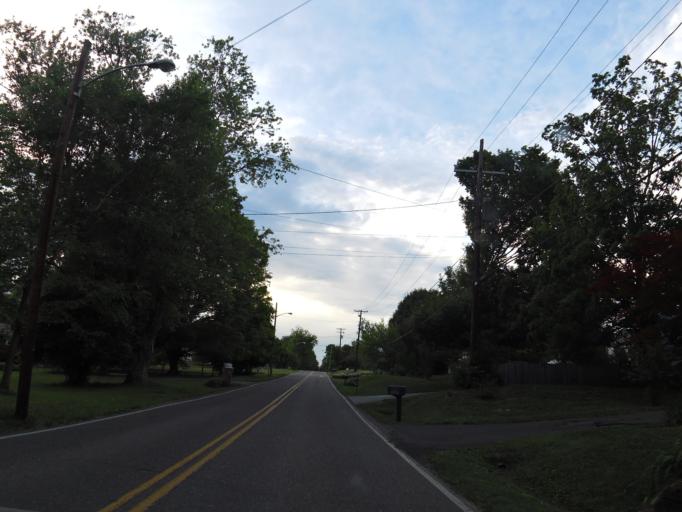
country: US
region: Tennessee
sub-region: Knox County
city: Knoxville
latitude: 36.0362
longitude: -83.9058
